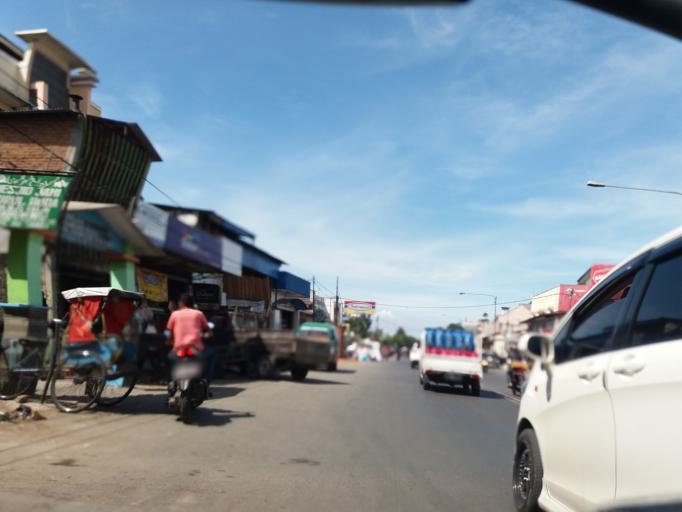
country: ID
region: West Java
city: Bandung
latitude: -6.9258
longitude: 107.5895
